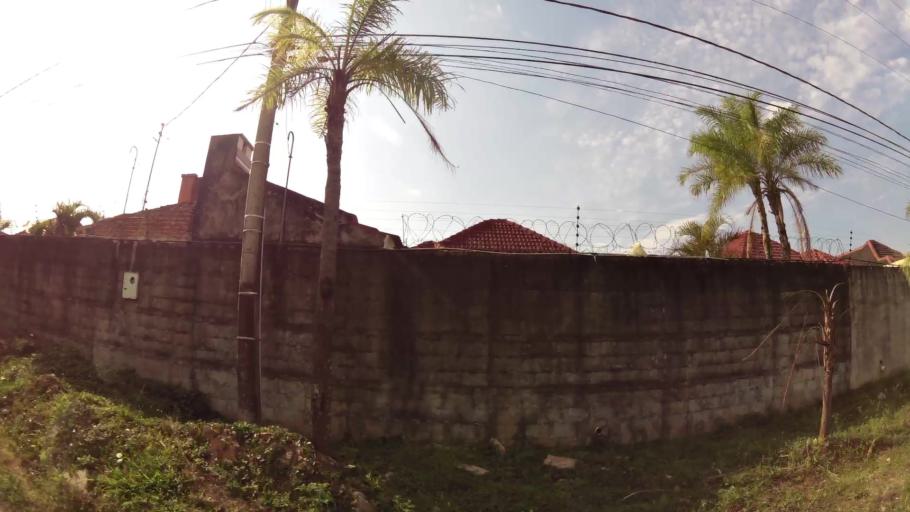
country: BO
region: Santa Cruz
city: Santa Cruz de la Sierra
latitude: -17.7236
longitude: -63.1737
